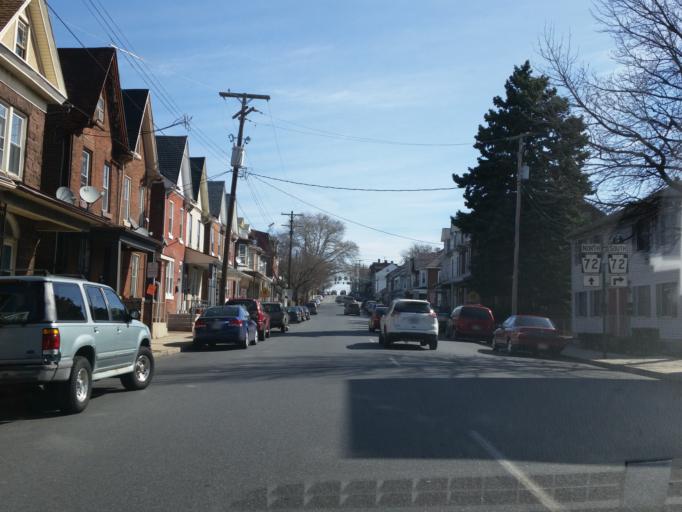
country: US
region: Pennsylvania
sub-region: Lebanon County
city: Pleasant Hill
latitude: 40.3363
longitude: -76.4297
